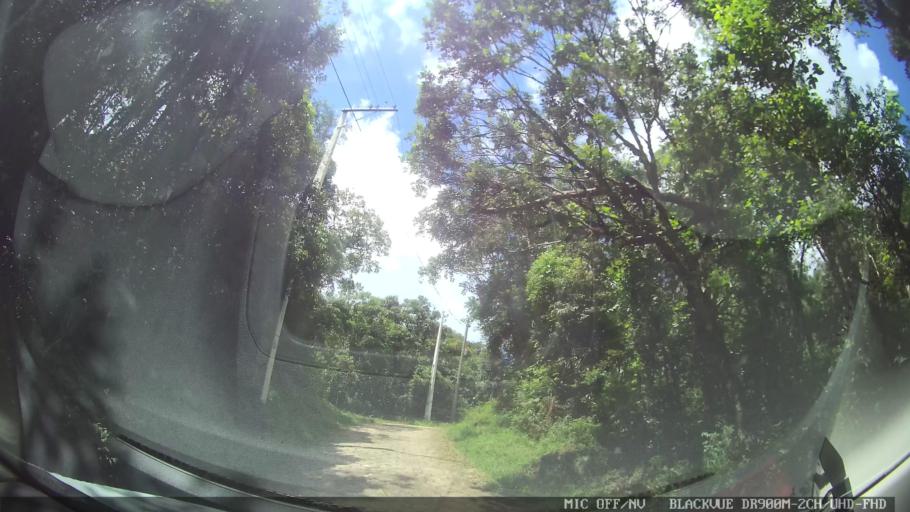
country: BR
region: Minas Gerais
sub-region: Extrema
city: Extrema
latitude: -22.8878
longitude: -46.3156
